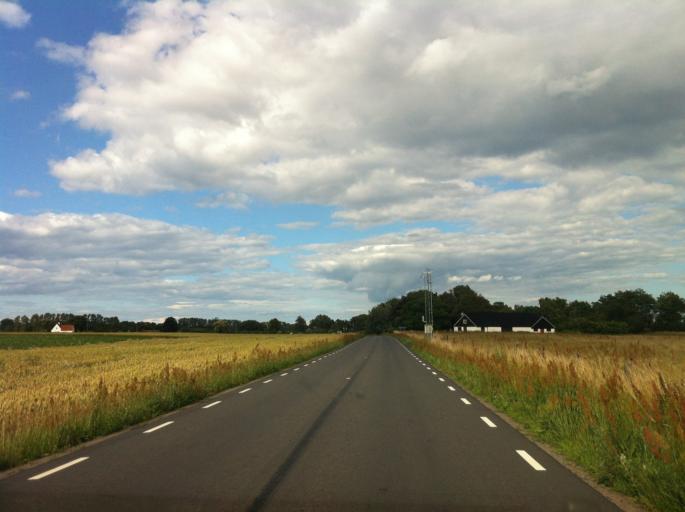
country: SE
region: Skane
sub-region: Simrishamns Kommun
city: Simrishamn
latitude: 55.4363
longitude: 14.2309
